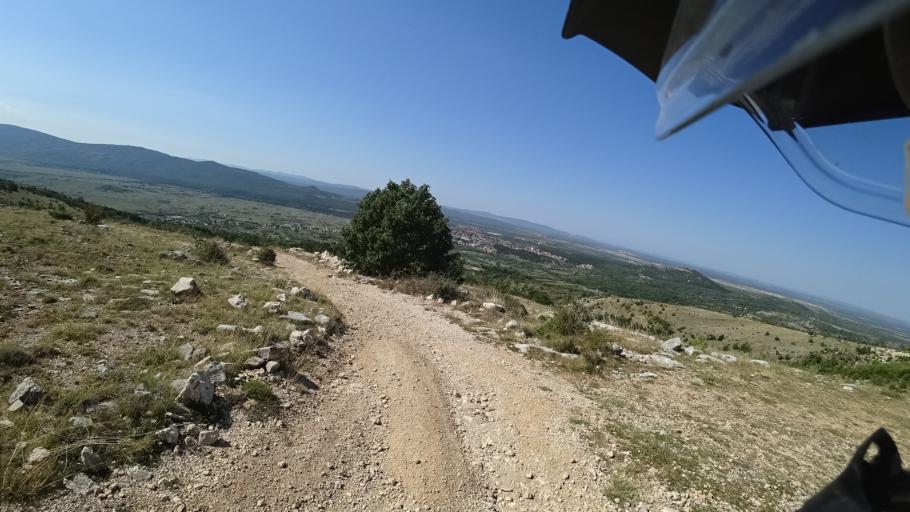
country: HR
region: Sibensko-Kniniska
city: Drnis
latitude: 43.8801
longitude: 16.1800
